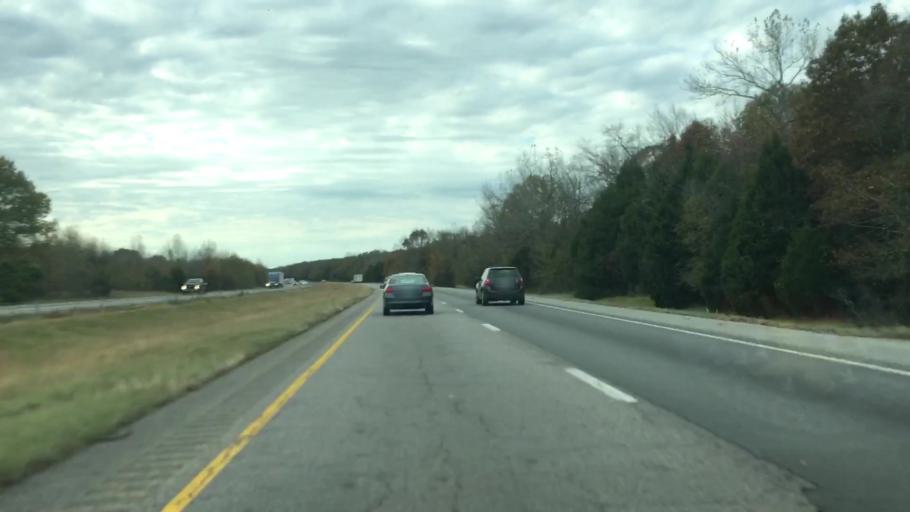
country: US
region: Arkansas
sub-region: Faulkner County
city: Conway
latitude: 35.1571
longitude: -92.5668
